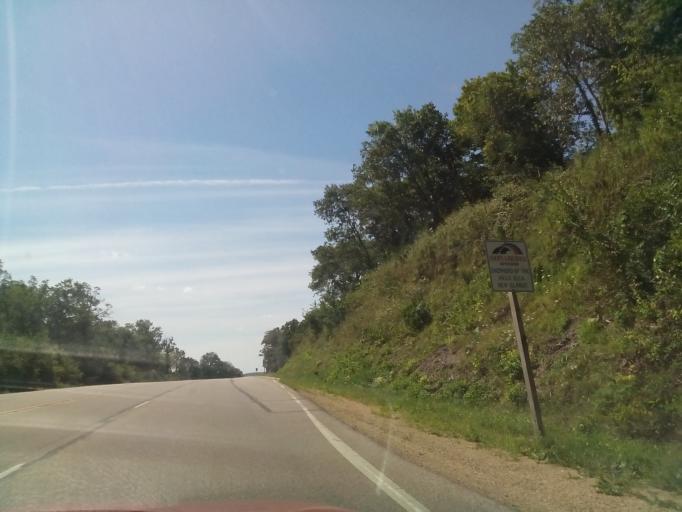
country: US
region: Wisconsin
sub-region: Green County
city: New Glarus
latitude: 42.7877
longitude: -89.6283
